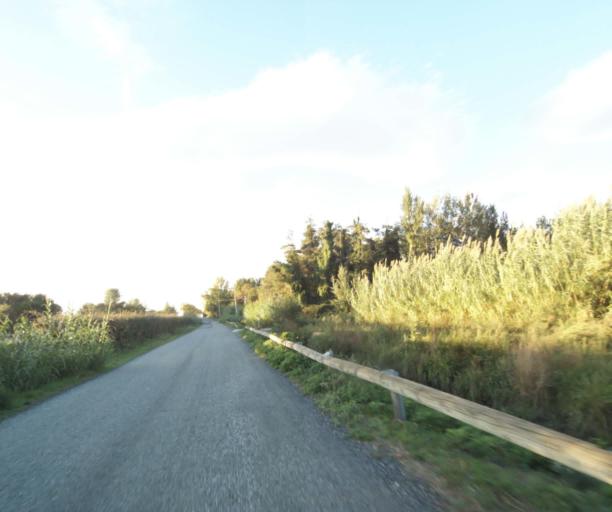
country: FR
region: Languedoc-Roussillon
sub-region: Departement des Pyrenees-Orientales
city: Latour-Bas-Elne
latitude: 42.5746
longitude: 2.9958
